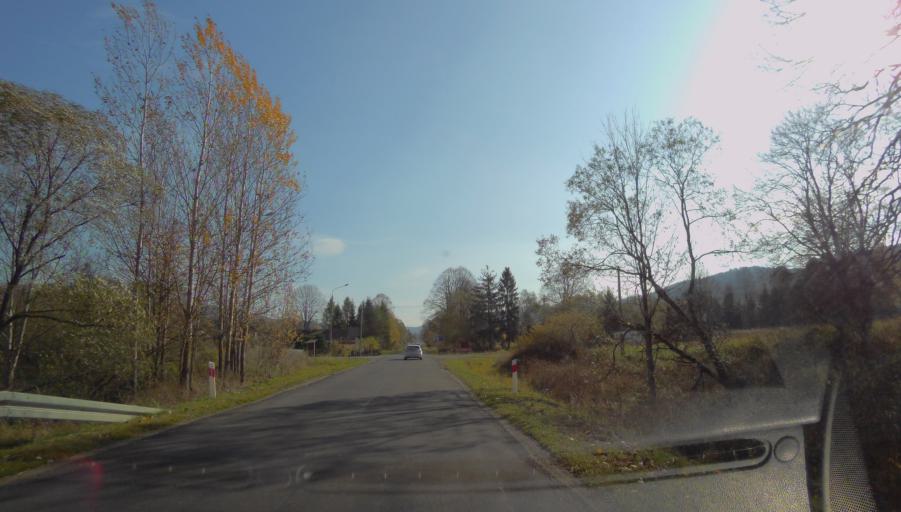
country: PL
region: Subcarpathian Voivodeship
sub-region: Powiat sanocki
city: Komancza
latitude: 49.2315
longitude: 22.1586
